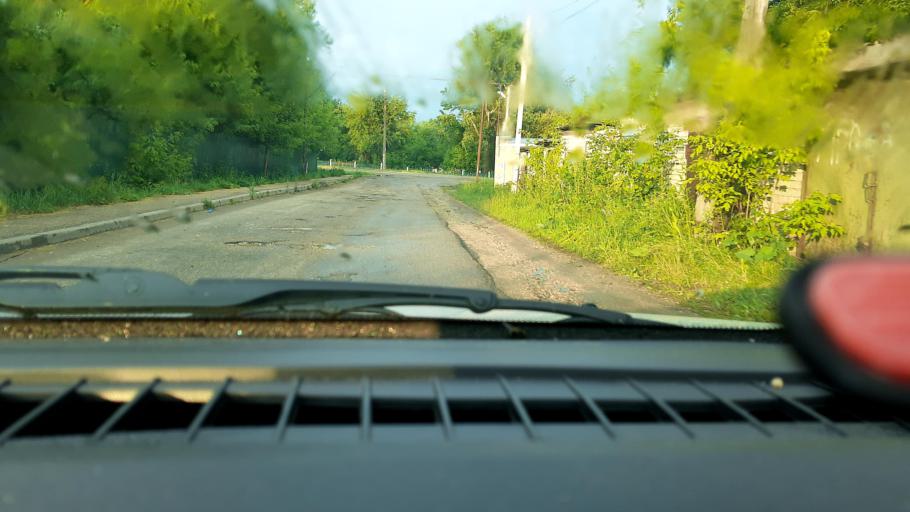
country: RU
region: Nizjnij Novgorod
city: Lukoyanov
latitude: 55.0416
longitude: 44.4962
